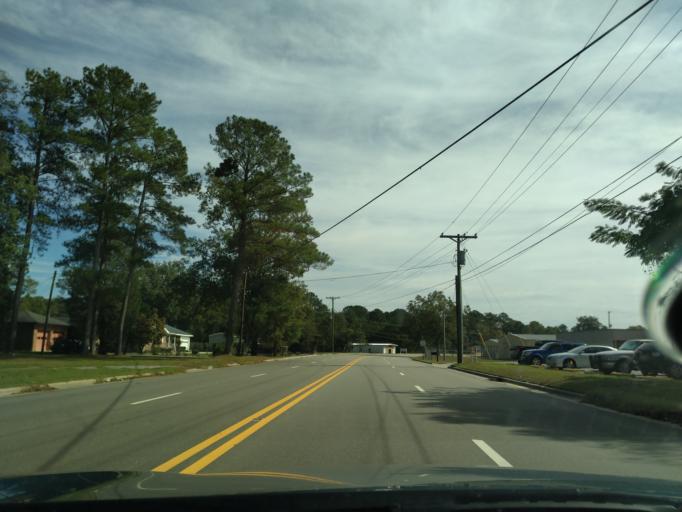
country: US
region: North Carolina
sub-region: Beaufort County
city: River Road
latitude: 35.5203
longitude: -77.0061
